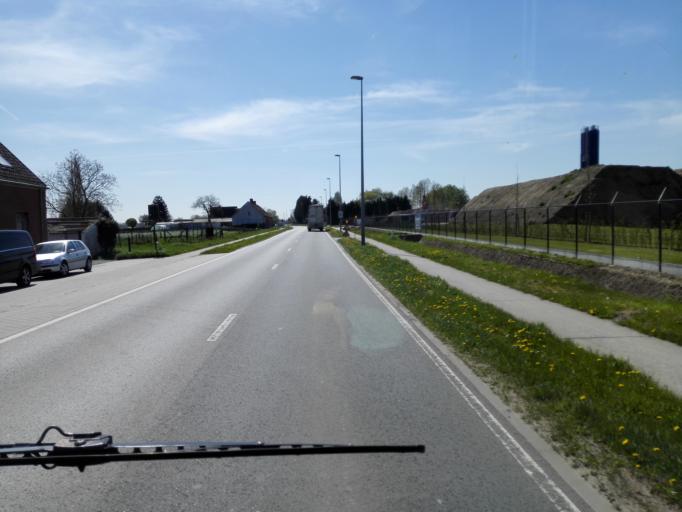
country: BE
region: Flanders
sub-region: Provincie West-Vlaanderen
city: Meulebeke
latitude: 50.9400
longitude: 3.2742
